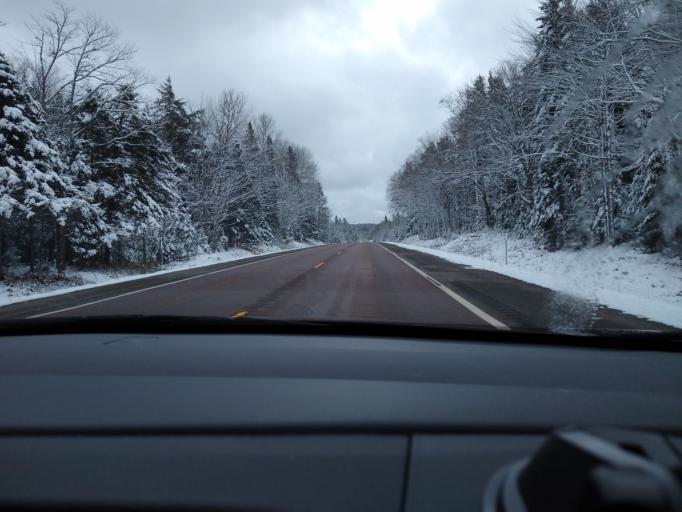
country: US
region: Wisconsin
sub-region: Vilas County
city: Eagle River
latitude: 46.2417
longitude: -89.0934
